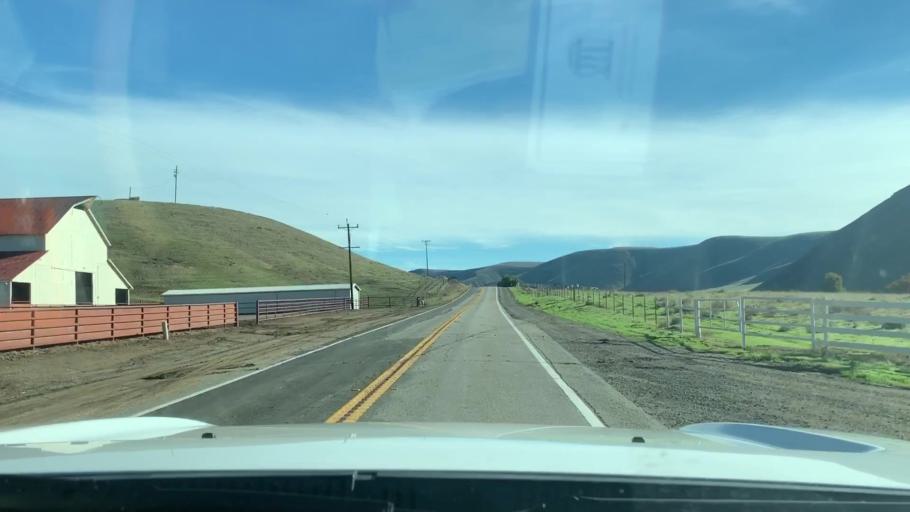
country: US
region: California
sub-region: Monterey County
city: King City
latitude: 36.1500
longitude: -120.9426
